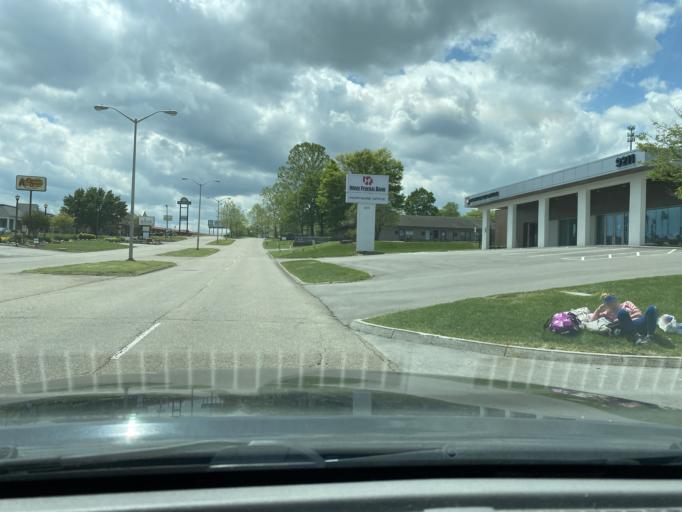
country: US
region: Tennessee
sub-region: Knox County
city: Farragut
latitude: 35.9195
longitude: -84.0927
